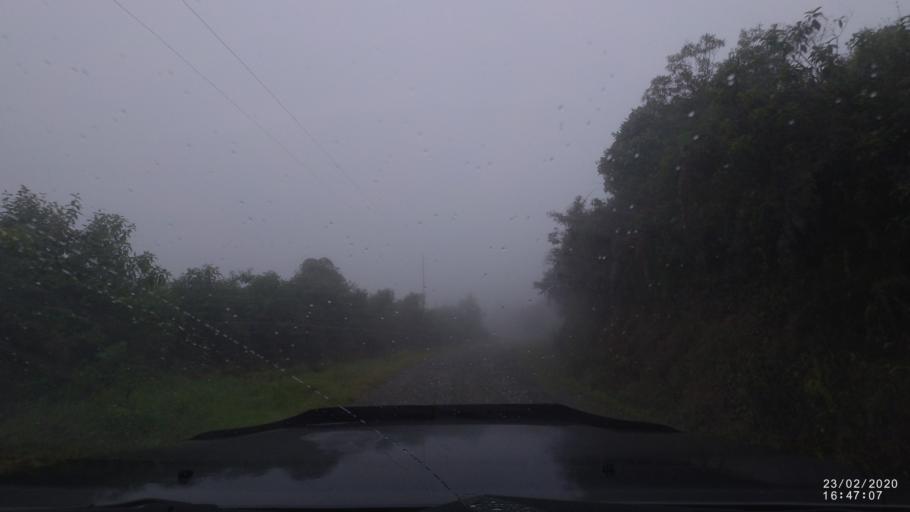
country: BO
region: Cochabamba
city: Colomi
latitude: -17.0897
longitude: -65.9943
